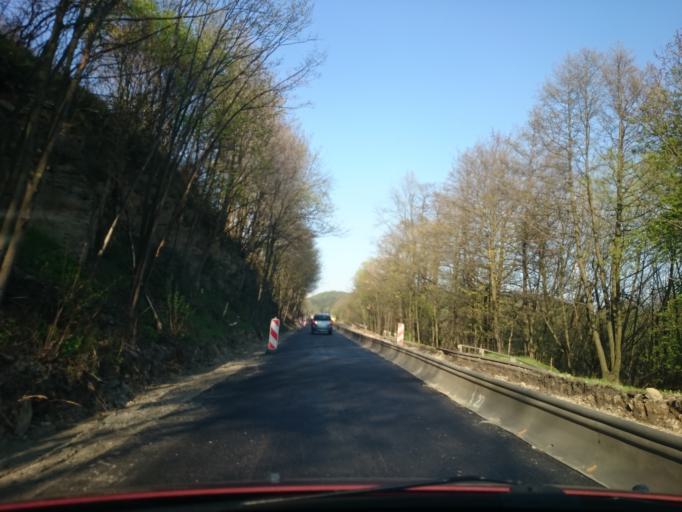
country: PL
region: Lower Silesian Voivodeship
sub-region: Powiat klodzki
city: Szczytna
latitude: 50.4098
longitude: 16.4362
